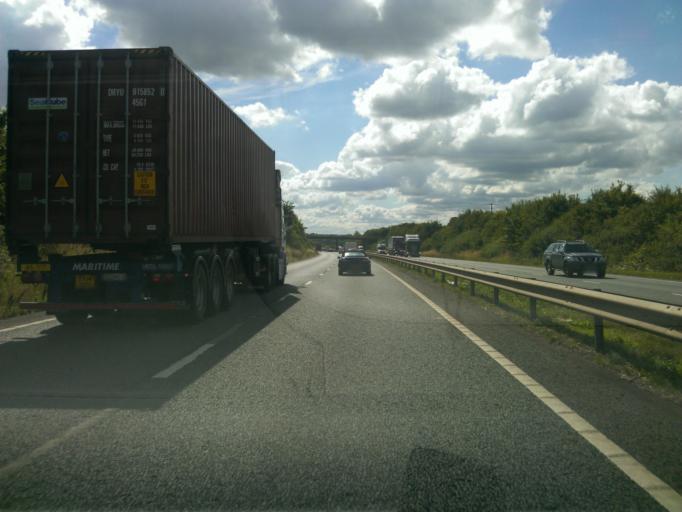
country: GB
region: England
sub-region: Leicestershire
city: Market Harborough
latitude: 52.4019
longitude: -0.9943
